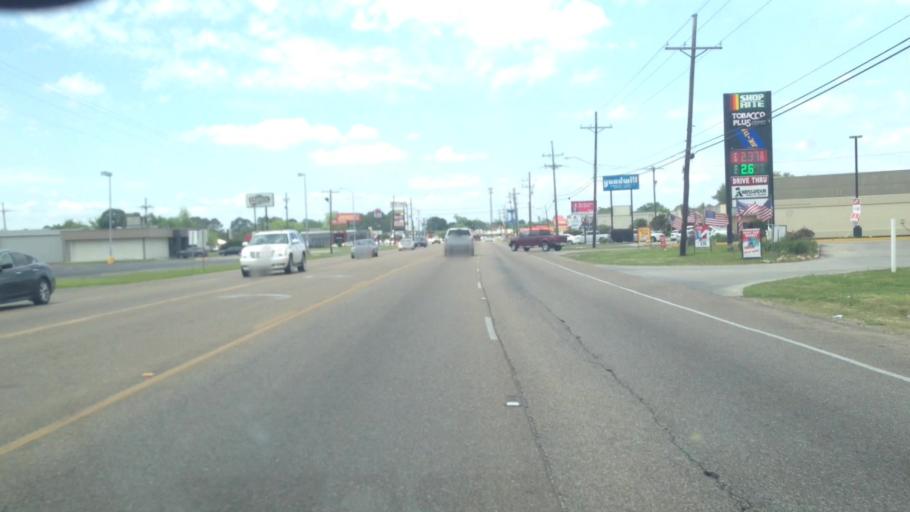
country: US
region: Louisiana
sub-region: Iberia Parish
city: New Iberia
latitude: 29.9865
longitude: -91.8218
